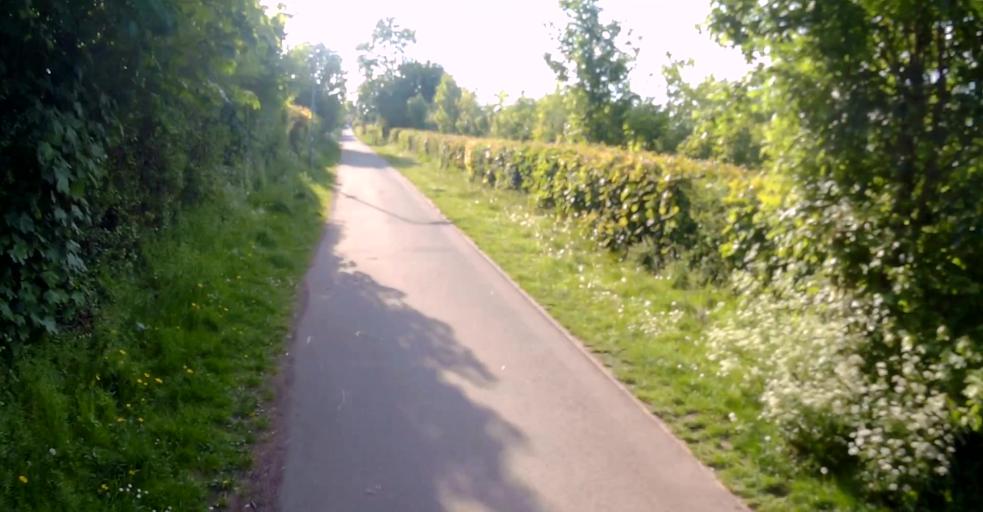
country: GB
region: England
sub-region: Hampshire
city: Basingstoke
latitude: 51.2294
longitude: -1.1378
